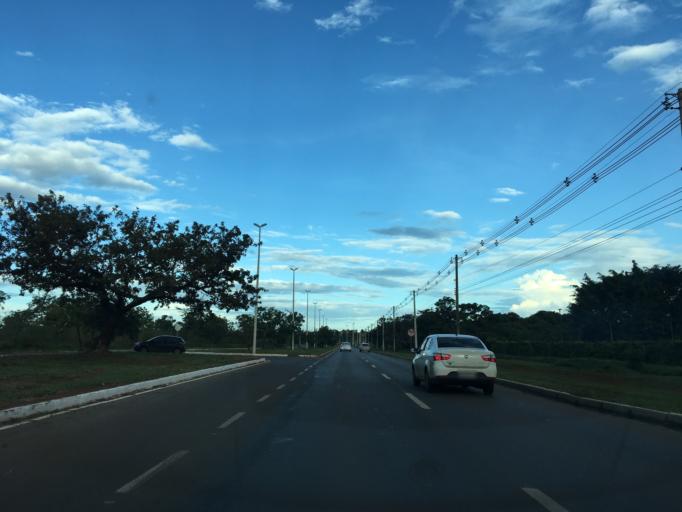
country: BR
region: Federal District
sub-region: Brasilia
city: Brasilia
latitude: -15.8148
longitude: -47.8524
